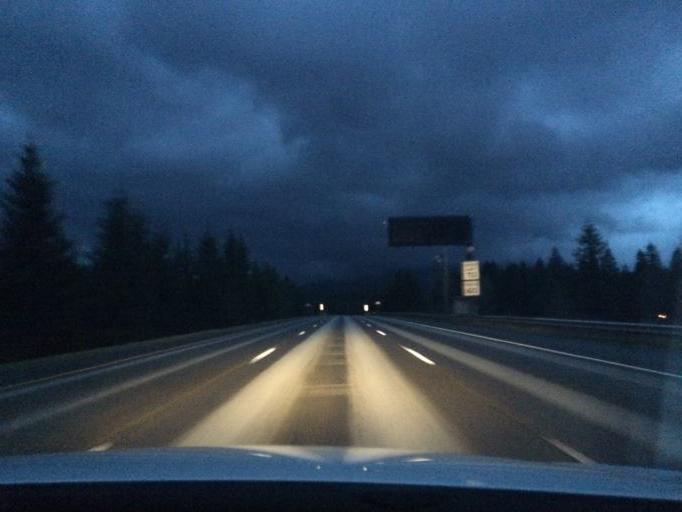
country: US
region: Washington
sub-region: King County
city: Tanner
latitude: 47.4732
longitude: -121.7475
